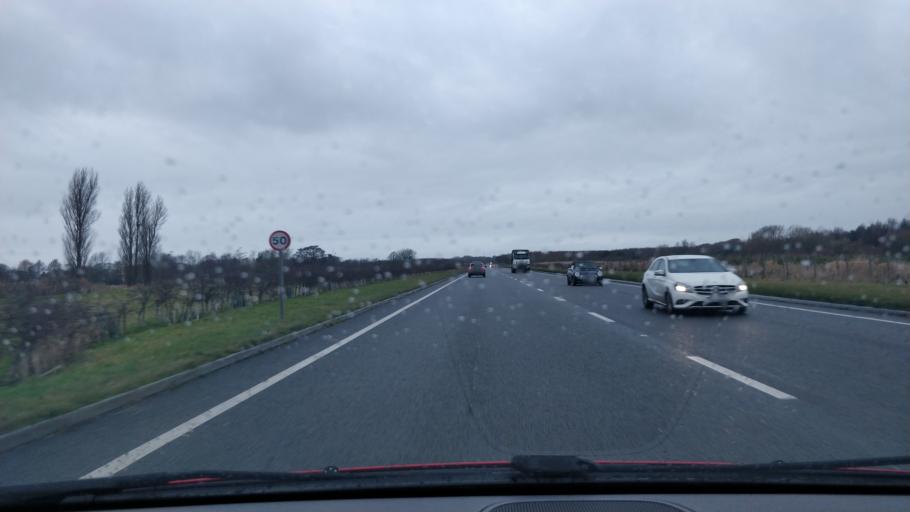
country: GB
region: England
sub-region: Sefton
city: Thornton
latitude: 53.5001
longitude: -2.9859
